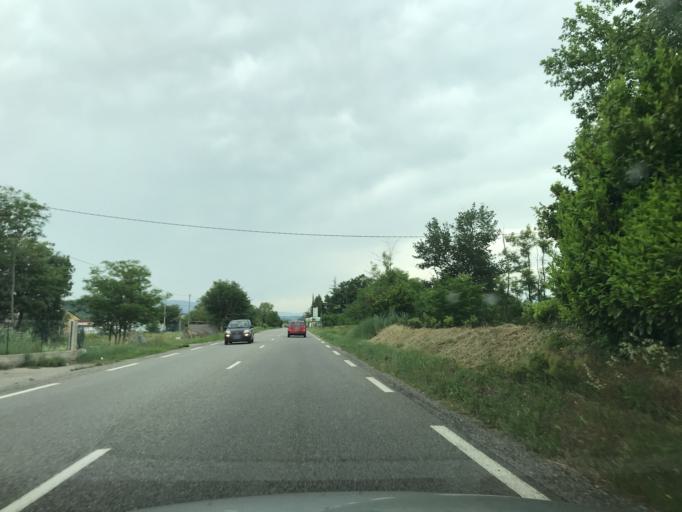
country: FR
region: Provence-Alpes-Cote d'Azur
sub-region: Departement des Alpes-de-Haute-Provence
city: Sisteron
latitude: 44.2137
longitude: 5.9254
